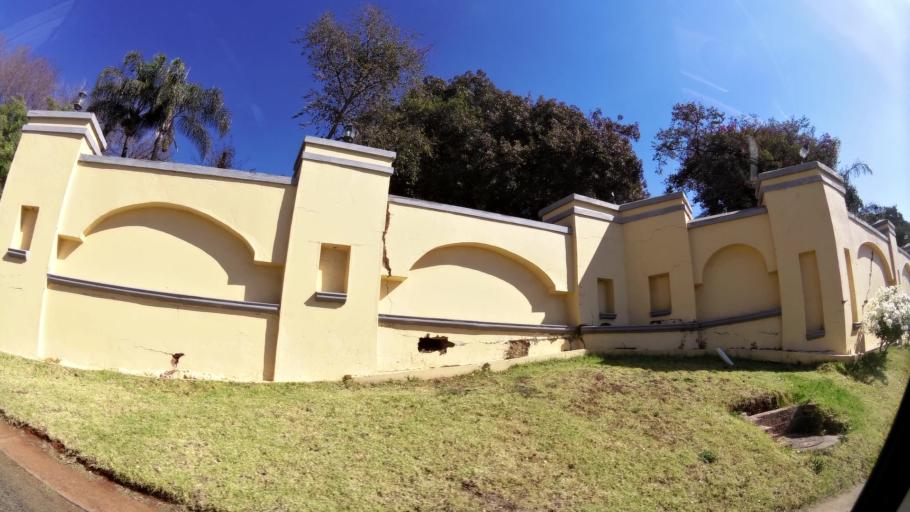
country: ZA
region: Gauteng
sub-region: City of Tshwane Metropolitan Municipality
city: Pretoria
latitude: -25.7848
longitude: 28.2507
